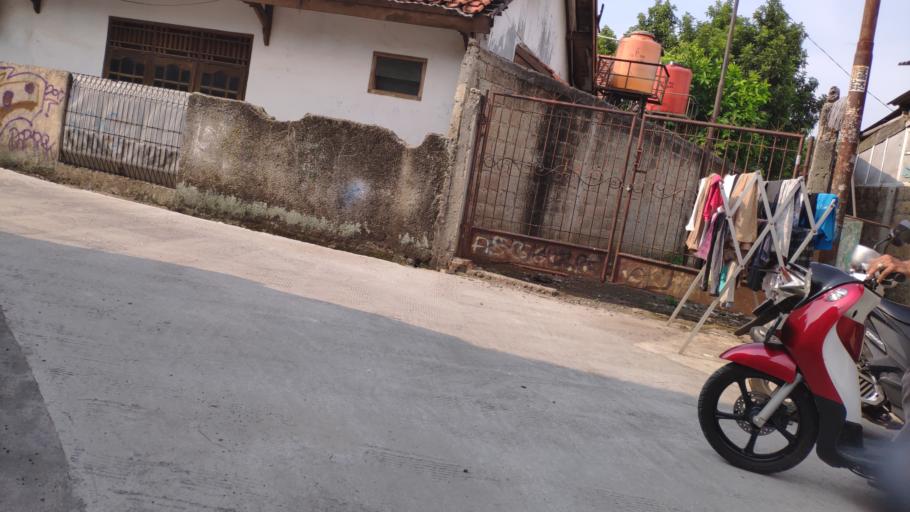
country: ID
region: West Java
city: Pamulang
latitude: -6.3277
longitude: 106.7935
